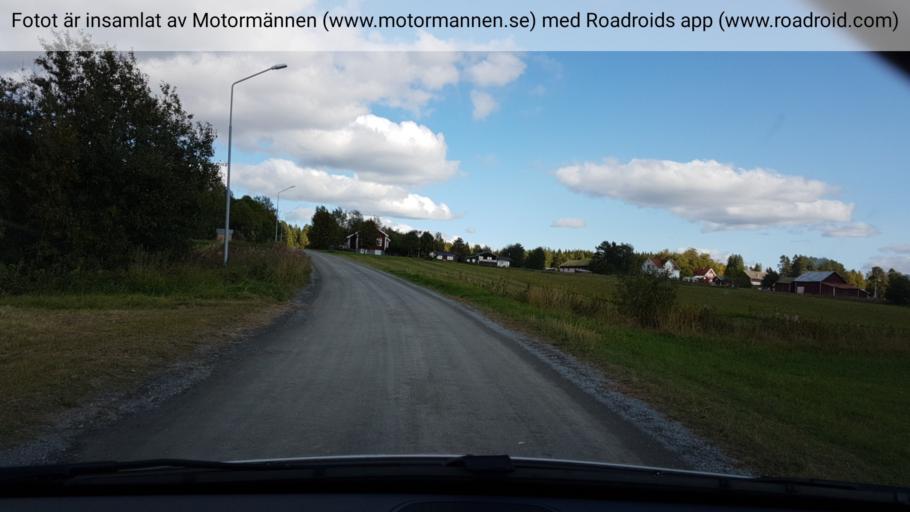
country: SE
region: Jaemtland
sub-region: Bergs Kommun
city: Hoverberg
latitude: 63.0393
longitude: 14.4566
